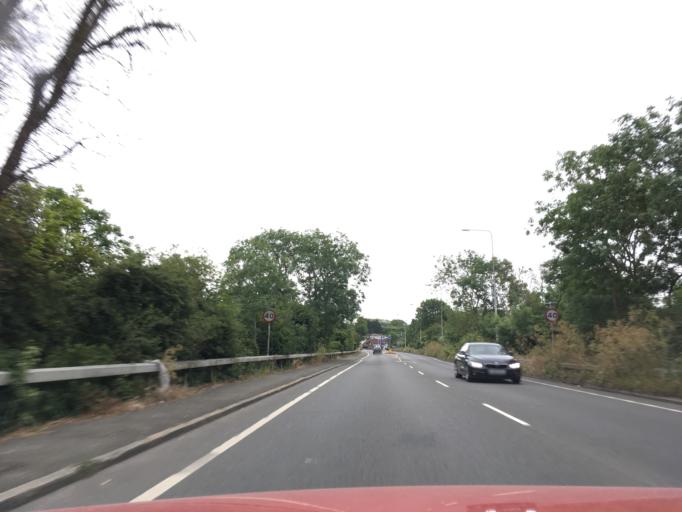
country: GB
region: England
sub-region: Central Bedfordshire
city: Houghton Regis
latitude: 51.9046
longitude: -0.5482
